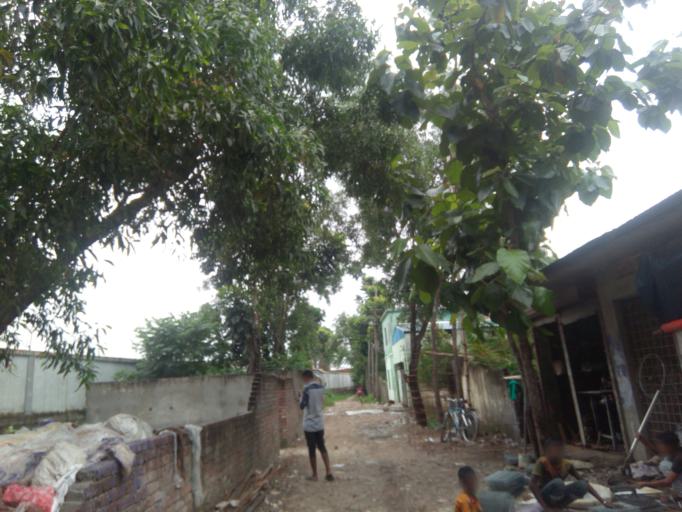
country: BD
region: Dhaka
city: Azimpur
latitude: 23.7452
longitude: 90.3521
